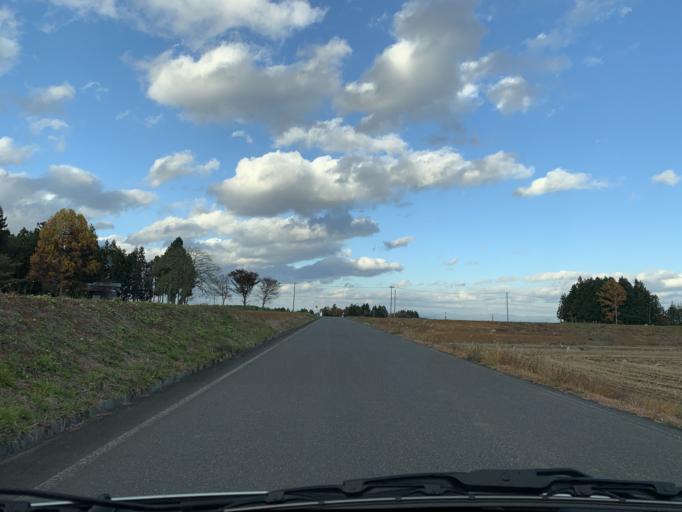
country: JP
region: Iwate
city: Mizusawa
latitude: 39.1059
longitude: 141.0220
